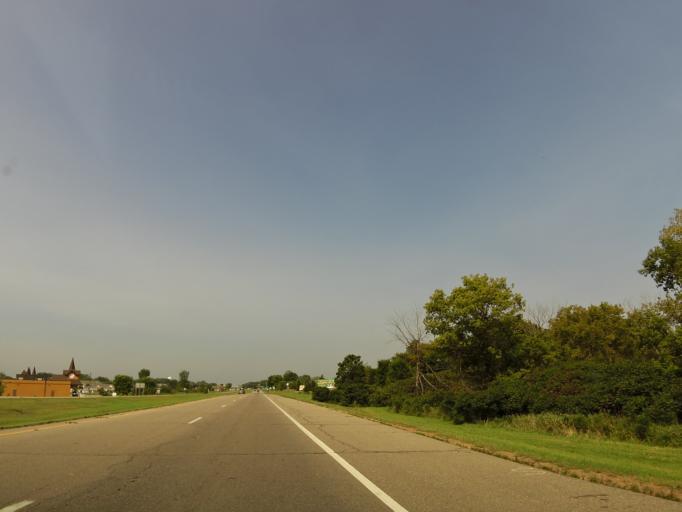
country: US
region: Minnesota
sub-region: Carver County
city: Norwood Young America
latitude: 44.7683
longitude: -93.9098
